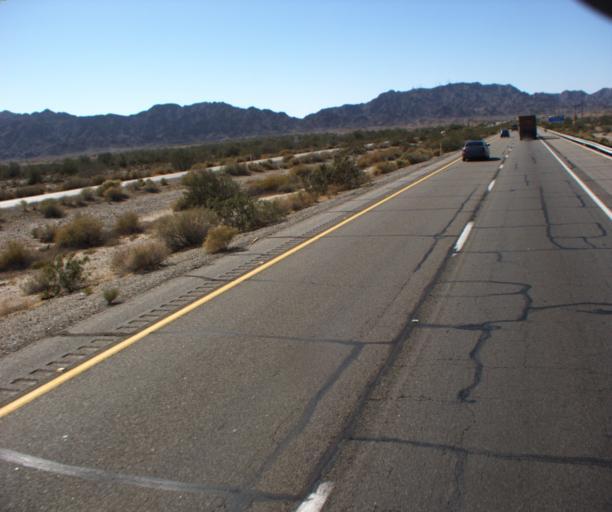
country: US
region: Arizona
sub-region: Yuma County
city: Wellton
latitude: 32.6635
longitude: -114.2686
